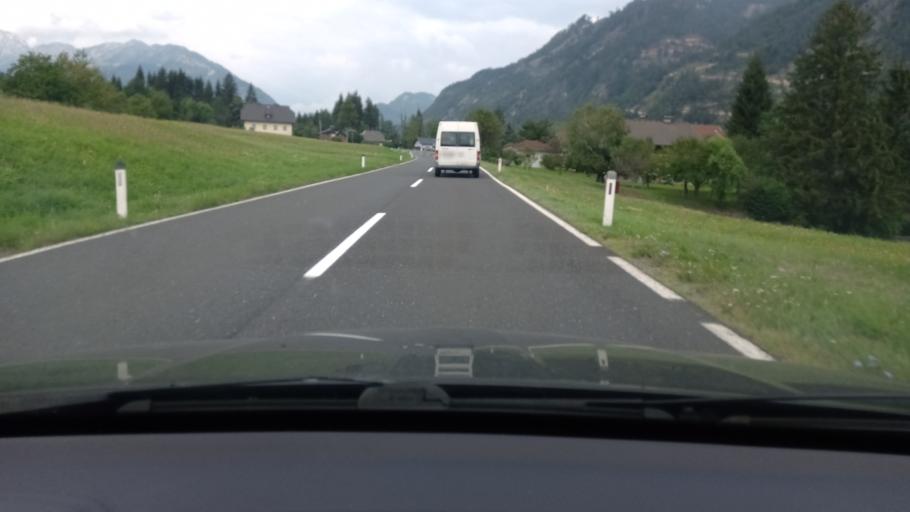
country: AT
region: Carinthia
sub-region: Politischer Bezirk Hermagor
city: Hermagor
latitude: 46.6648
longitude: 13.3059
